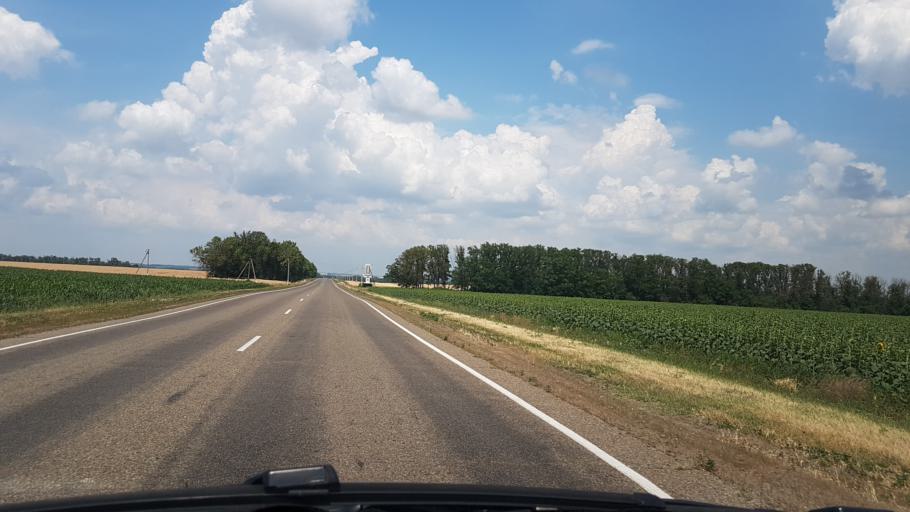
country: RU
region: Krasnodarskiy
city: Dmitriyevskaya
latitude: 45.6887
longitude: 40.7441
